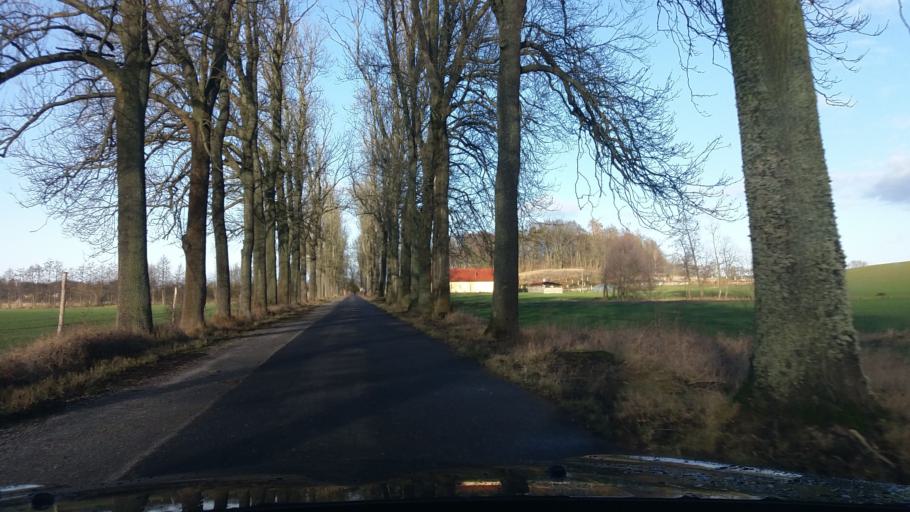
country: PL
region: West Pomeranian Voivodeship
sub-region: Powiat choszczenski
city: Drawno
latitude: 53.2084
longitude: 15.7741
